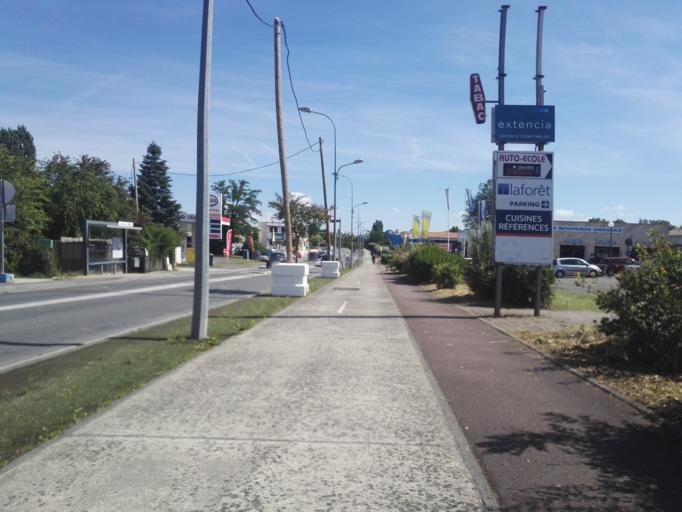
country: FR
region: Aquitaine
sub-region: Departement de la Gironde
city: Villenave-d'Ornon
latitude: 44.7697
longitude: -0.5787
